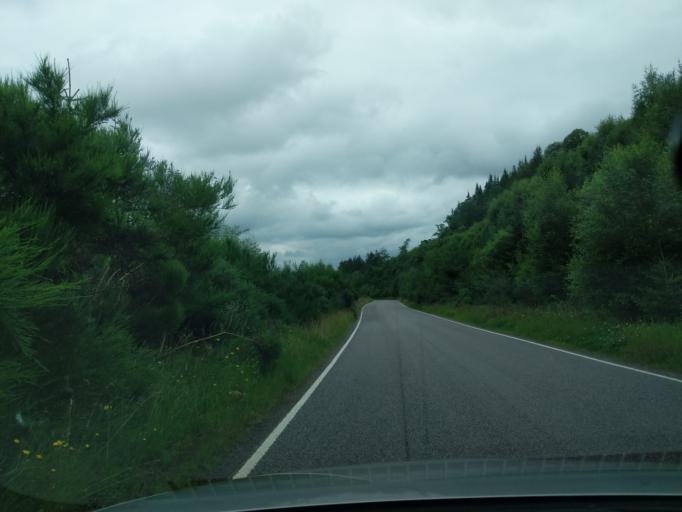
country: GB
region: Scotland
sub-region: Moray
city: Forres
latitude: 57.5193
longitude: -3.6799
